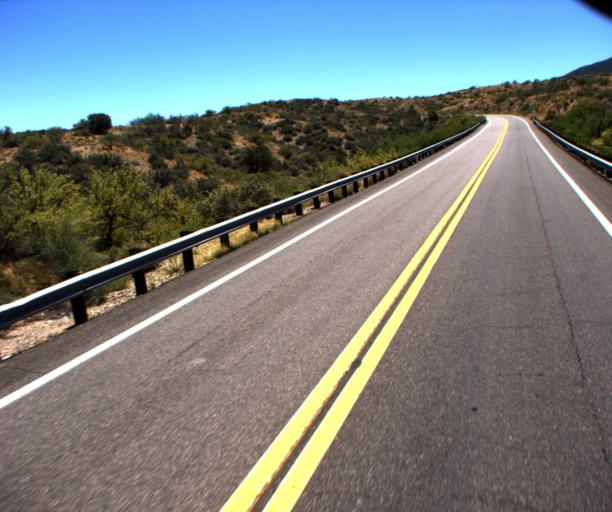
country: US
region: Arizona
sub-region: Gila County
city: Globe
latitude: 33.3295
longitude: -110.7313
